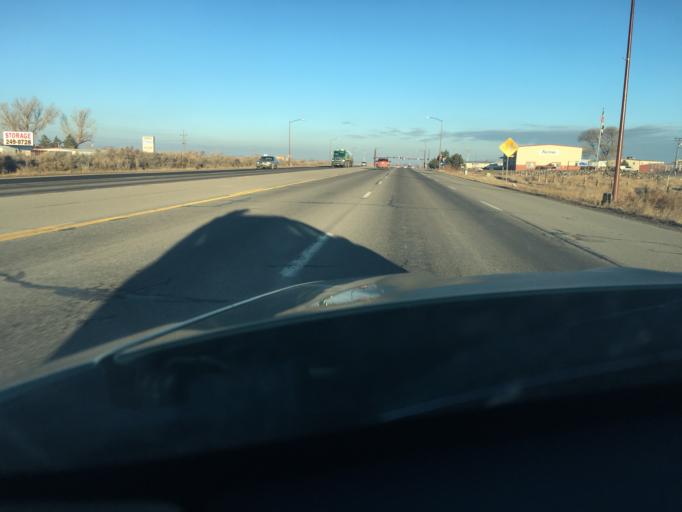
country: US
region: Colorado
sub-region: Montrose County
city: Montrose
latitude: 38.5013
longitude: -107.9025
